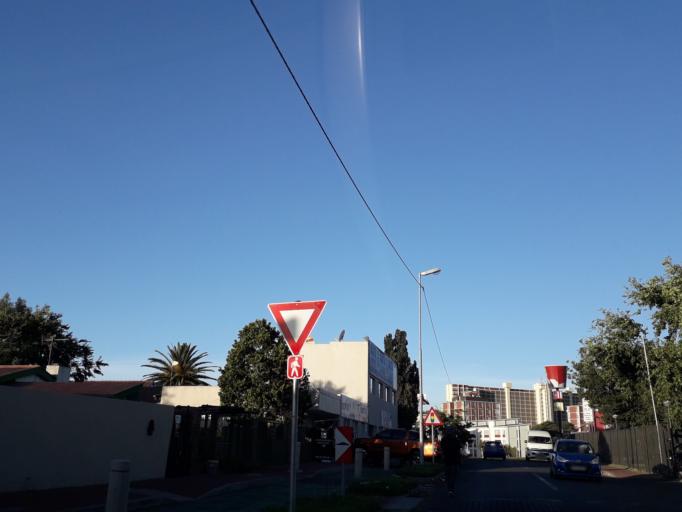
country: ZA
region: Gauteng
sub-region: City of Johannesburg Metropolitan Municipality
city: Johannesburg
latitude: -26.1748
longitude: 27.9791
